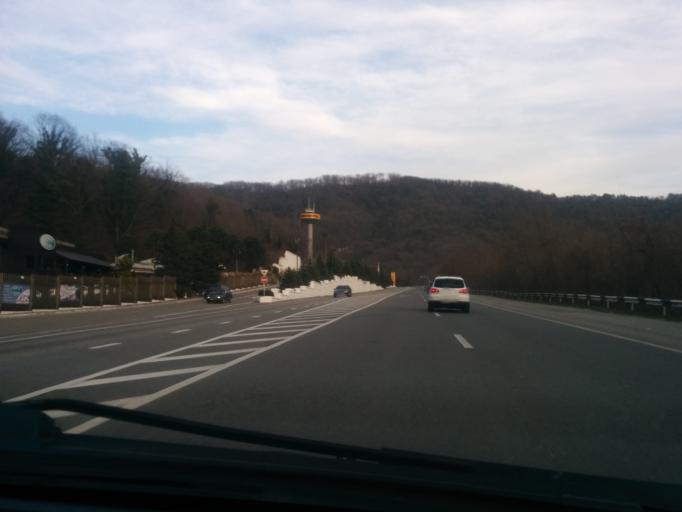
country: RU
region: Krasnodarskiy
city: Agoy
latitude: 44.1418
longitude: 39.0448
